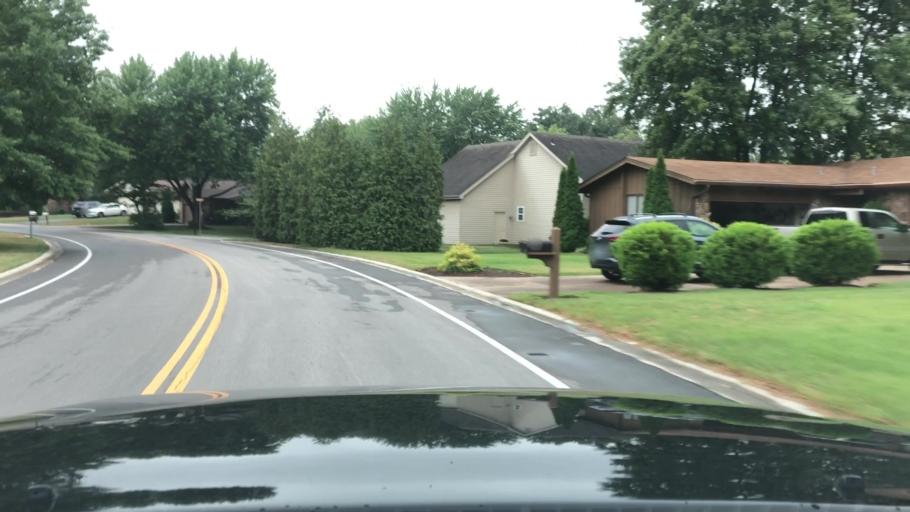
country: US
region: Missouri
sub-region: Saint Charles County
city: Lake Saint Louis
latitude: 38.7947
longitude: -90.8034
